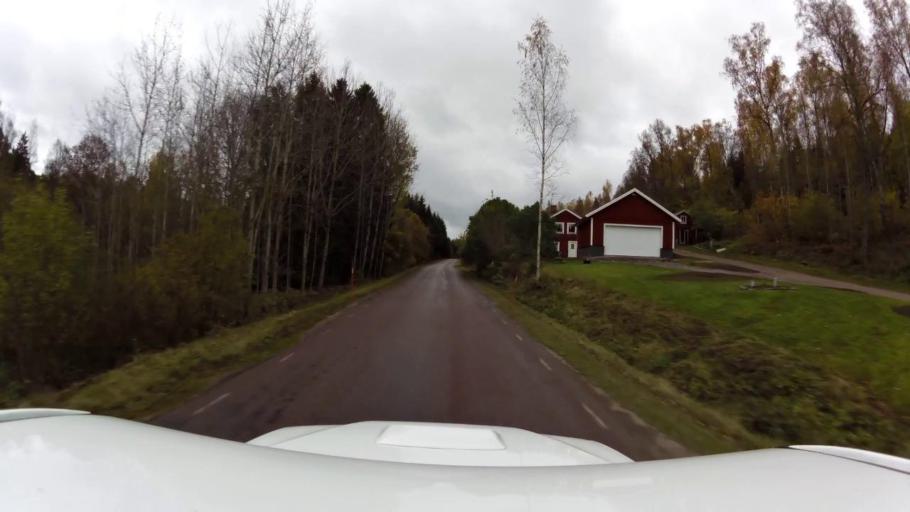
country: SE
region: OEstergoetland
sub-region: Linkopings Kommun
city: Ljungsbro
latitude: 58.5640
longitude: 15.5160
